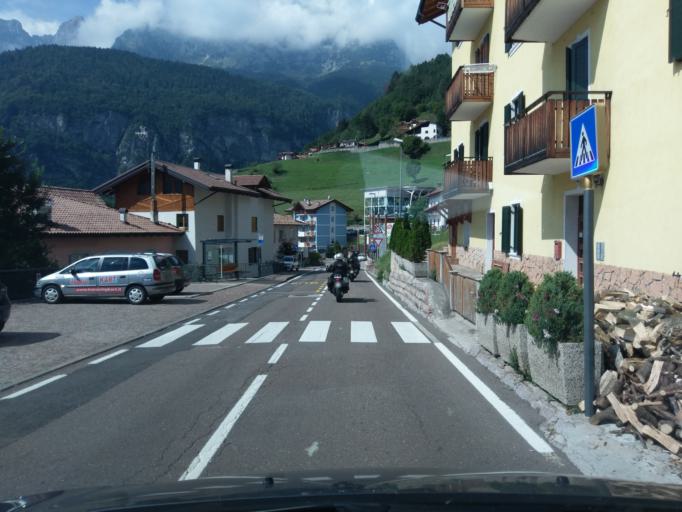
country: IT
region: Trentino-Alto Adige
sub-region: Provincia di Trento
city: Molveno
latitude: 46.1441
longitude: 10.9668
